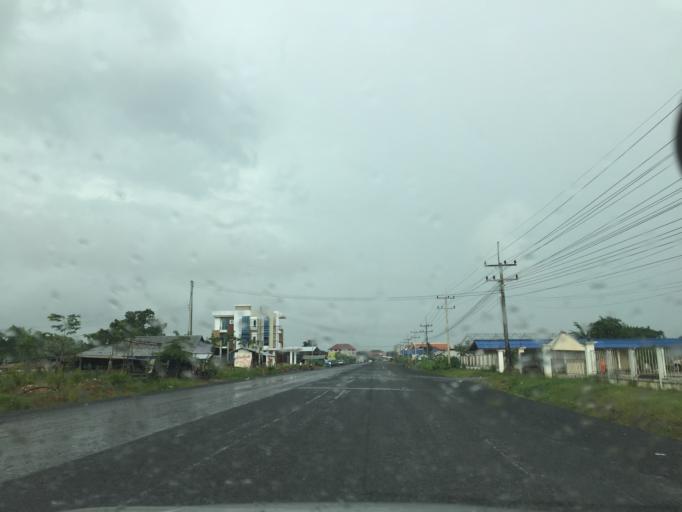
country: LA
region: Attapu
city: Attapu
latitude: 14.8250
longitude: 106.8086
